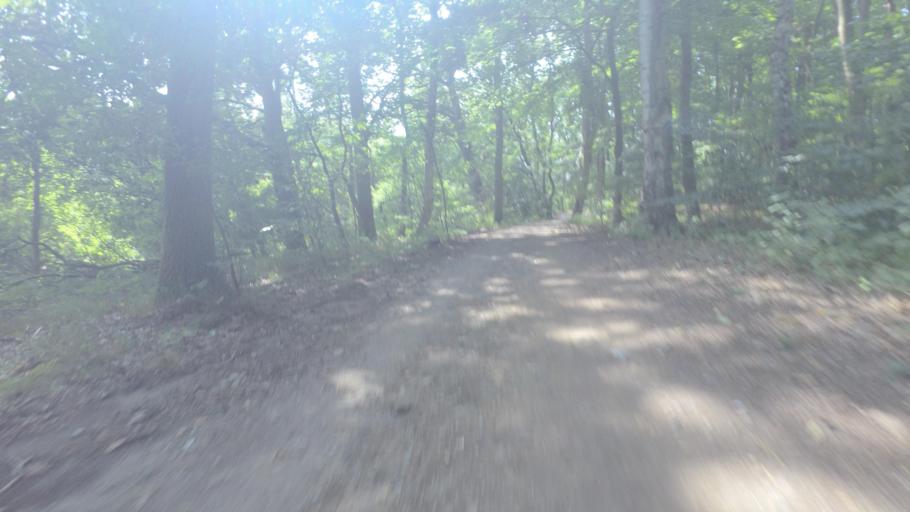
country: DE
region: Mecklenburg-Vorpommern
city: Waren
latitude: 53.5078
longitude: 12.6454
